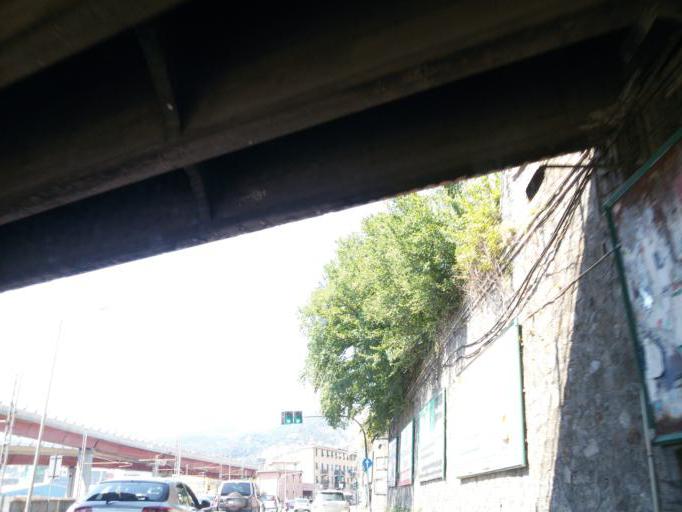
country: IT
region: Liguria
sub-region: Provincia di Genova
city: San Teodoro
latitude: 44.4173
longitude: 8.8597
